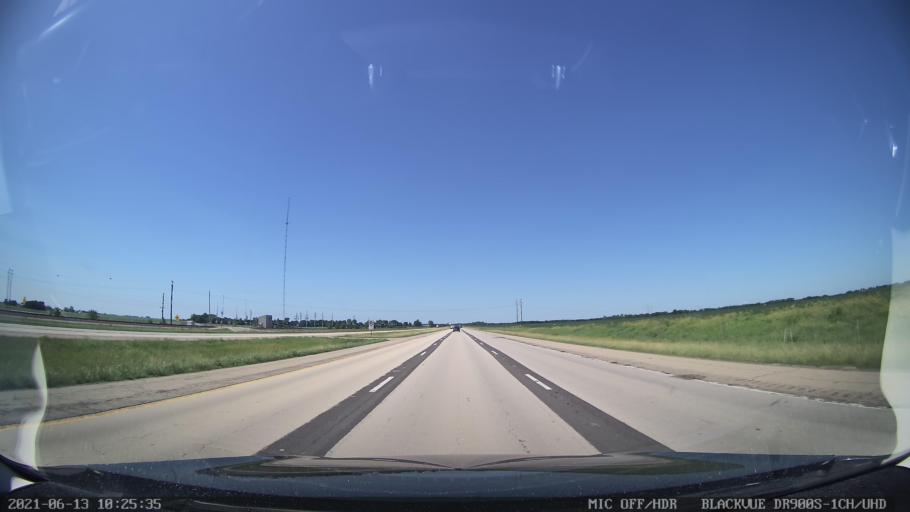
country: US
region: Illinois
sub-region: Sangamon County
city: Williamsville
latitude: 39.9936
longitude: -89.5121
